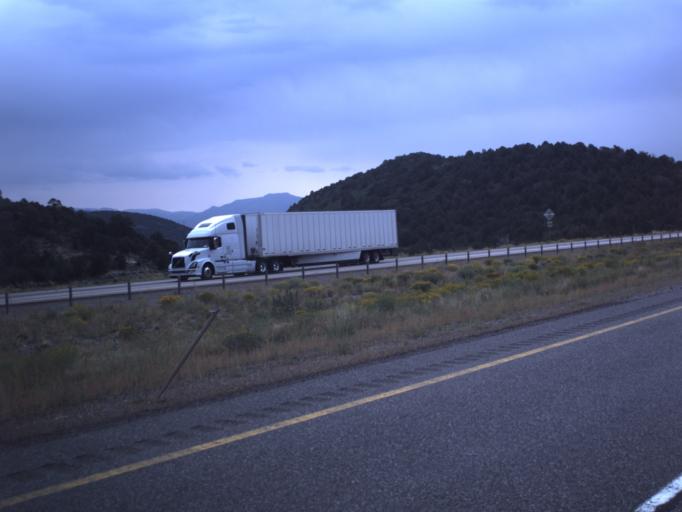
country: US
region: Utah
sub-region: Beaver County
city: Beaver
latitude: 38.5886
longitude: -112.4913
